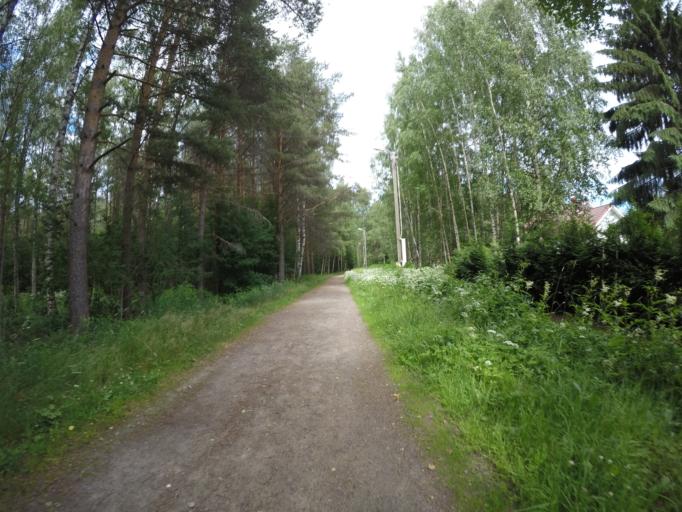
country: FI
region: Haeme
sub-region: Haemeenlinna
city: Parola
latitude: 61.0035
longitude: 24.3934
